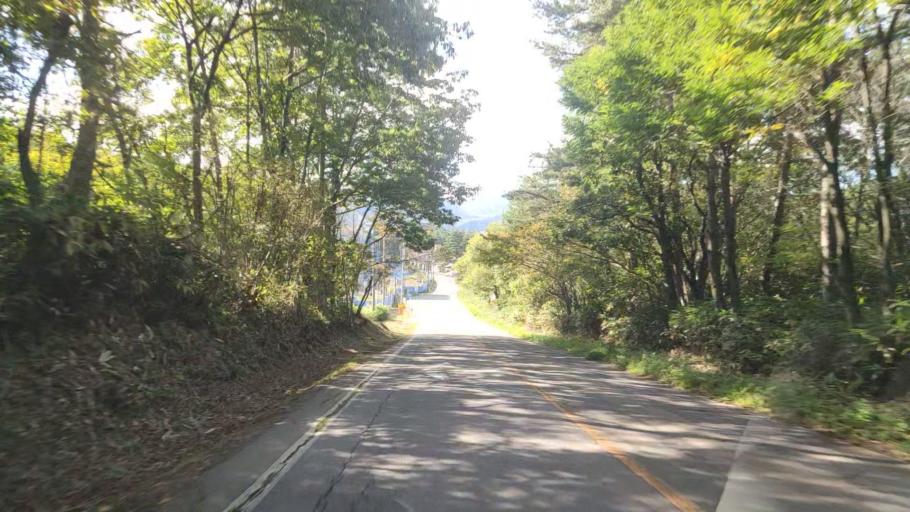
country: JP
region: Gunma
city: Nakanojomachi
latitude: 36.6210
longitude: 138.6163
